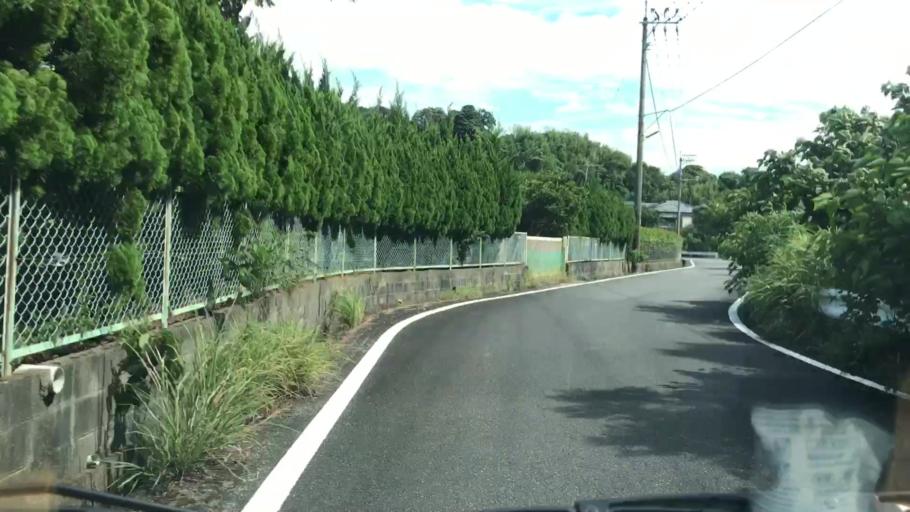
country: JP
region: Saga Prefecture
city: Saga-shi
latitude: 33.2299
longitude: 130.1778
